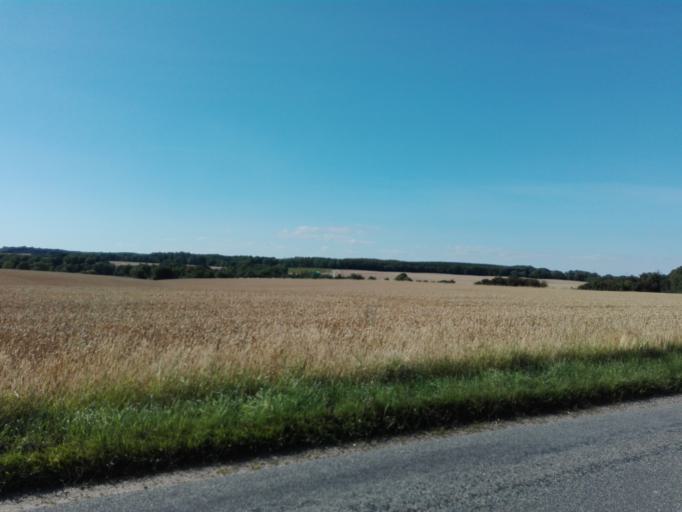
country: DK
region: Central Jutland
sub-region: Odder Kommune
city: Odder
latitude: 55.9589
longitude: 10.1143
